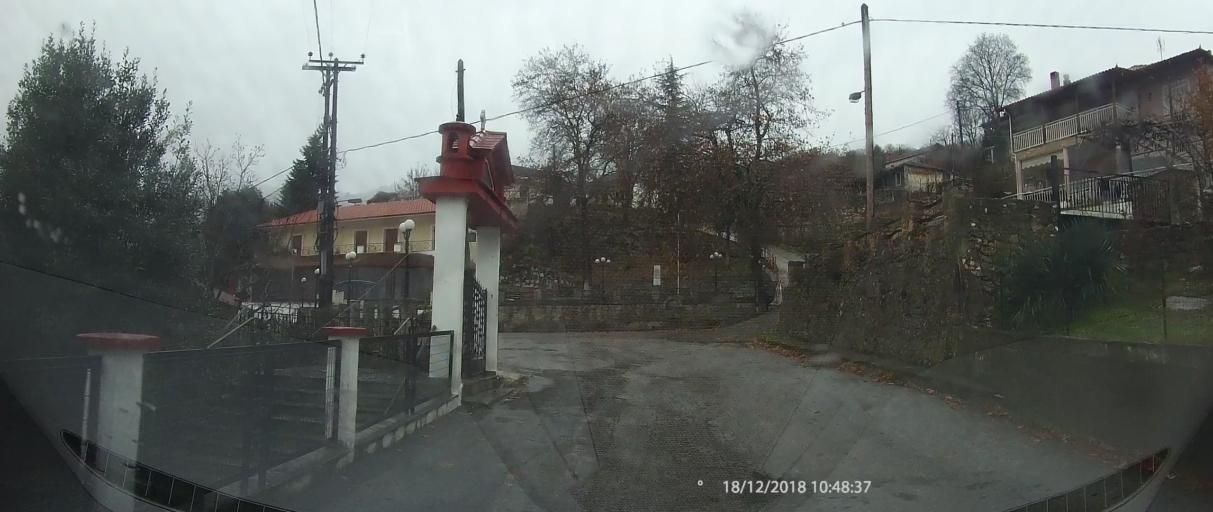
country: GR
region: Central Macedonia
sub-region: Nomos Pierias
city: Kato Milia
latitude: 40.1805
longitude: 22.3306
